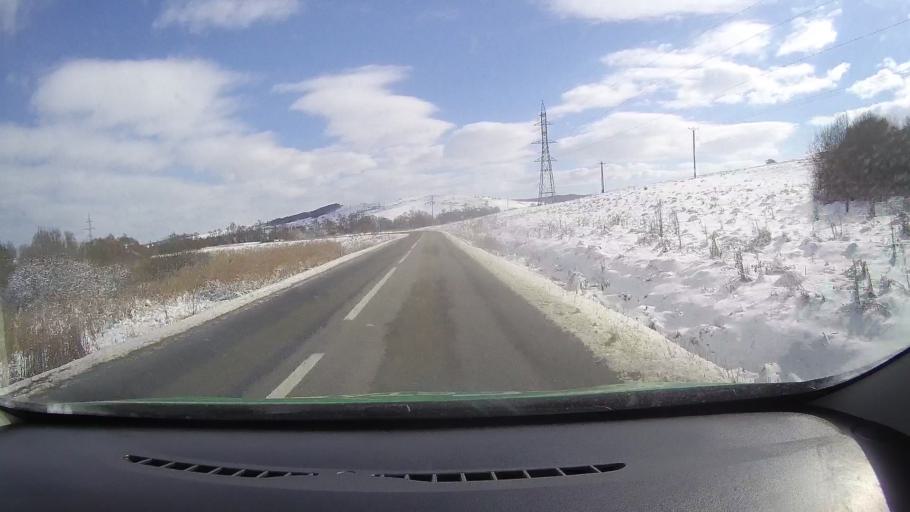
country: RO
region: Sibiu
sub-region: Comuna Barghis
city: Barghis
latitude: 45.9622
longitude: 24.5624
